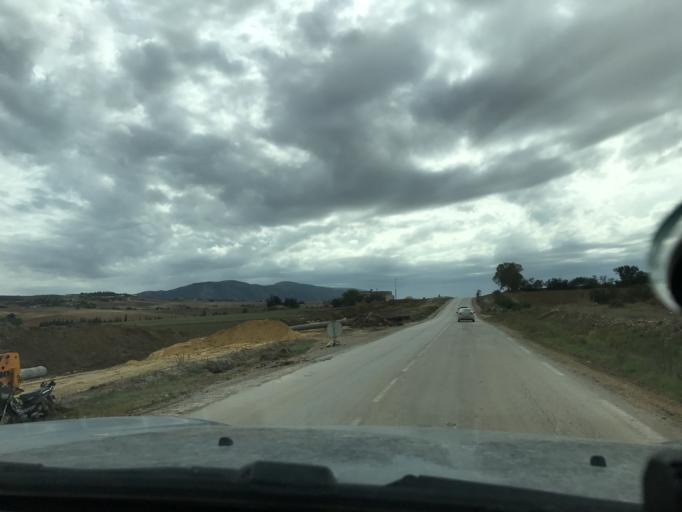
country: TN
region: Silyanah
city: Bu `Aradah
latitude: 36.1721
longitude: 9.6577
